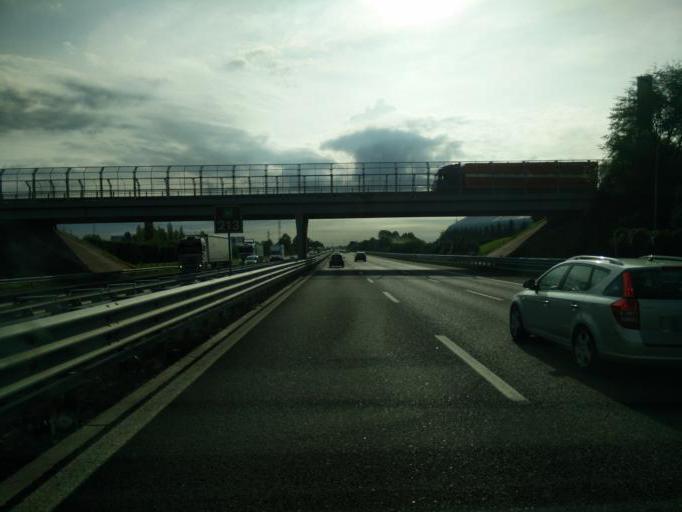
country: IT
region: Lombardy
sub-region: Provincia di Brescia
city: Folzano
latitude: 45.5147
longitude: 10.2077
